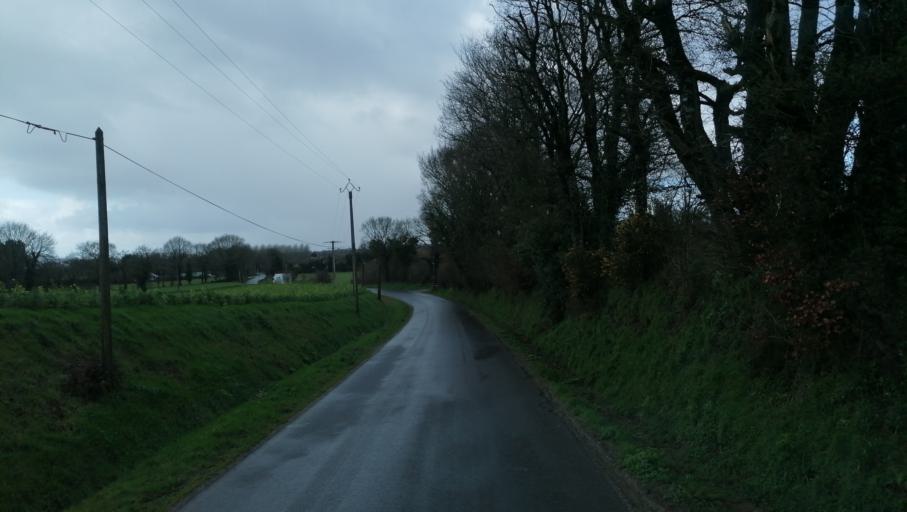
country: FR
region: Brittany
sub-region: Departement des Cotes-d'Armor
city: Lanrodec
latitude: 48.4914
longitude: -3.0034
